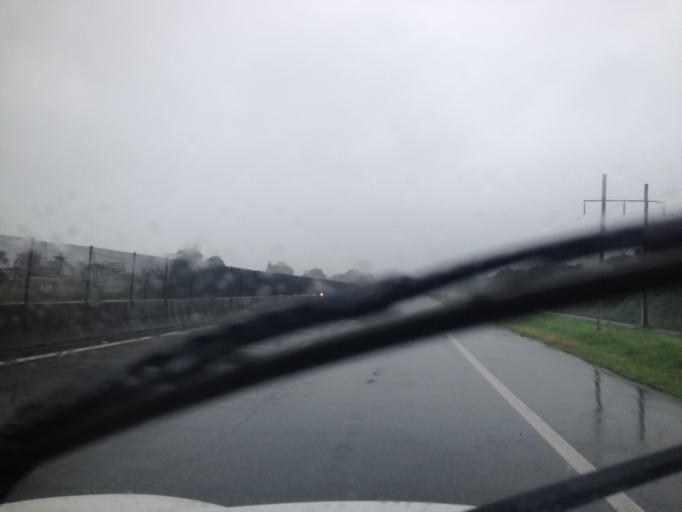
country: BR
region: Sao Paulo
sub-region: Mongagua
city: Mongagua
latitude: -24.0668
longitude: -46.5720
